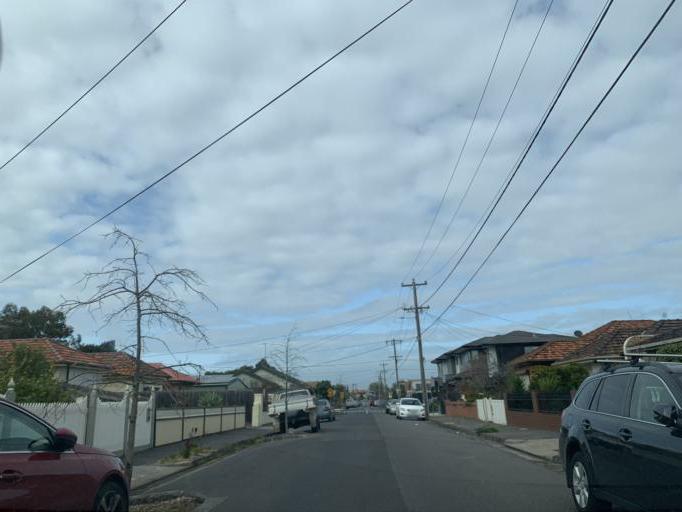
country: AU
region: Victoria
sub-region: Moreland
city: Coburg North
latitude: -37.7376
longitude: 144.9563
